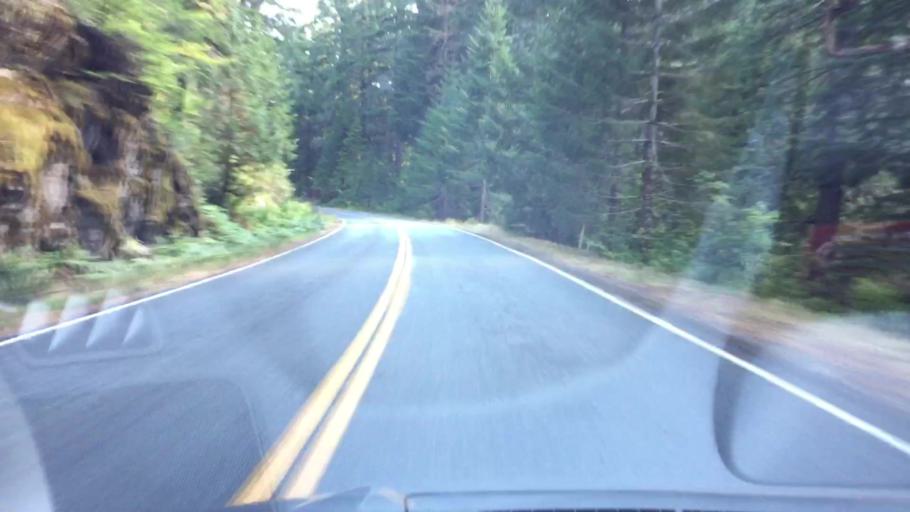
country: US
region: Washington
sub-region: Pierce County
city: Buckley
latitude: 46.7191
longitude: -121.5776
